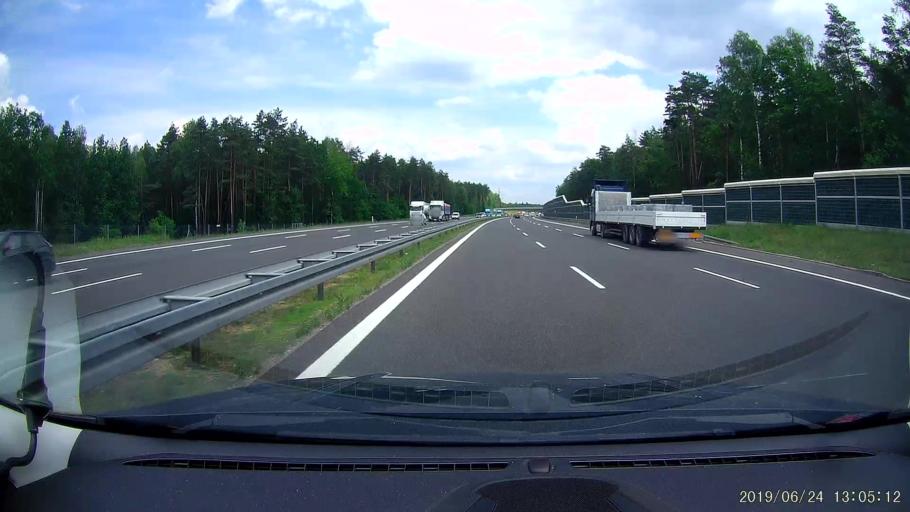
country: PL
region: Silesian Voivodeship
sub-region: Powiat rybnicki
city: Stanowice
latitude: 50.1013
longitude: 18.6668
